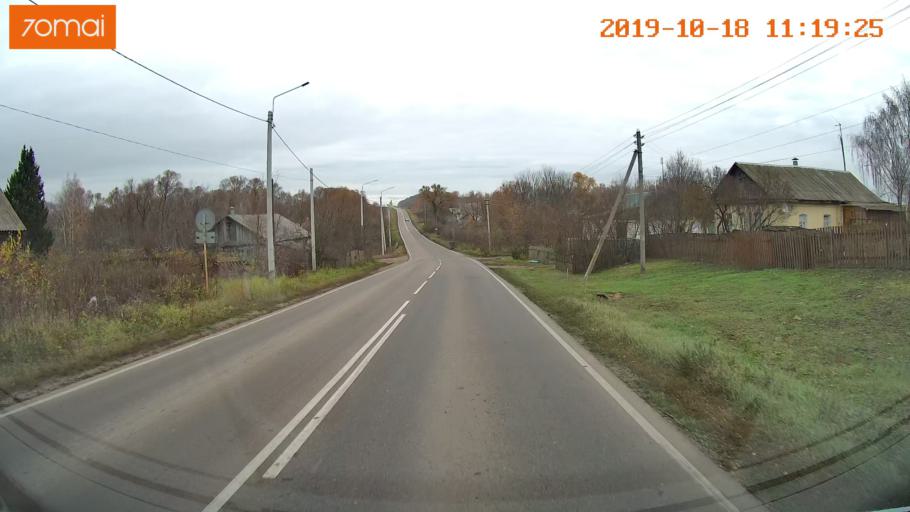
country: RU
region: Tula
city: Kimovsk
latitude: 54.0462
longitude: 38.5538
